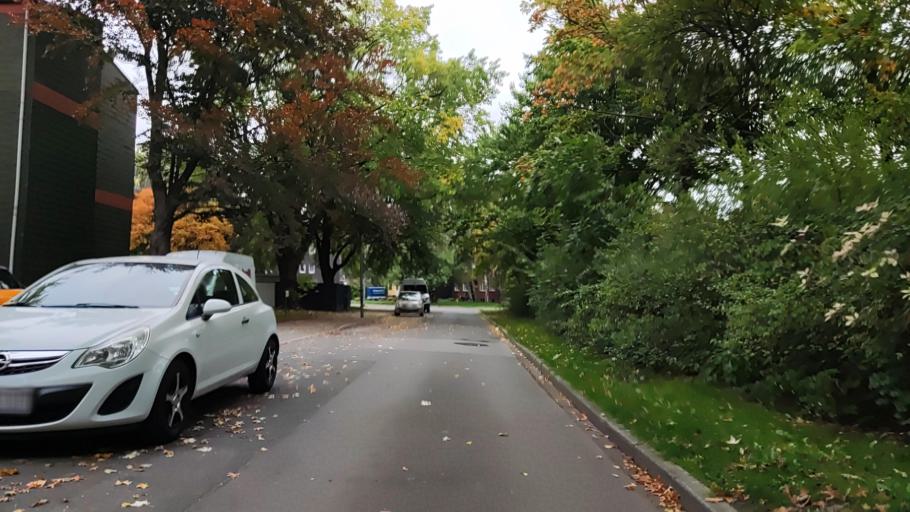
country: DE
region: North Rhine-Westphalia
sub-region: Regierungsbezirk Arnsberg
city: Herne
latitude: 51.5486
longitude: 7.2002
